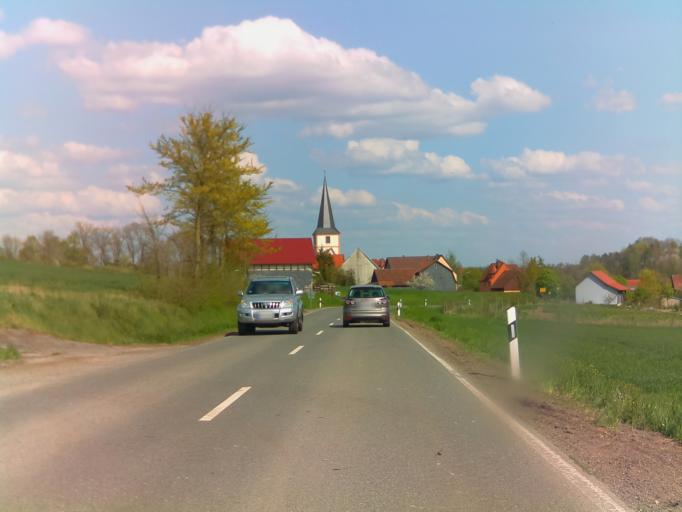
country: DE
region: Thuringia
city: Hildburghausen
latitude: 50.3493
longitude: 10.7360
